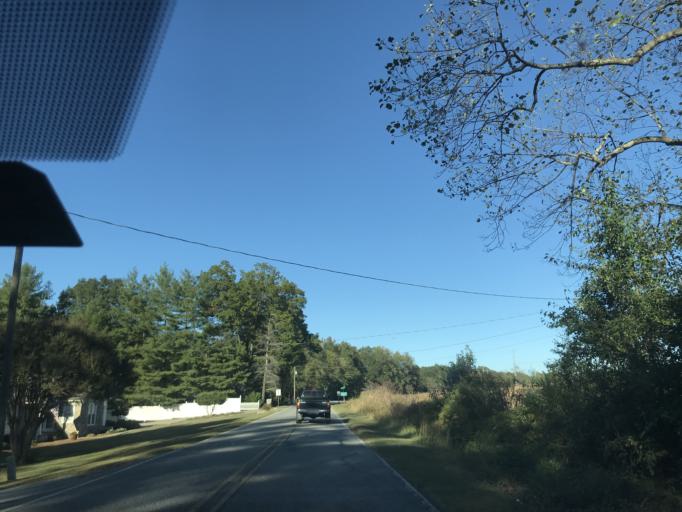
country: US
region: South Carolina
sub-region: Spartanburg County
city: Mayo
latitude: 35.1076
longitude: -81.8340
